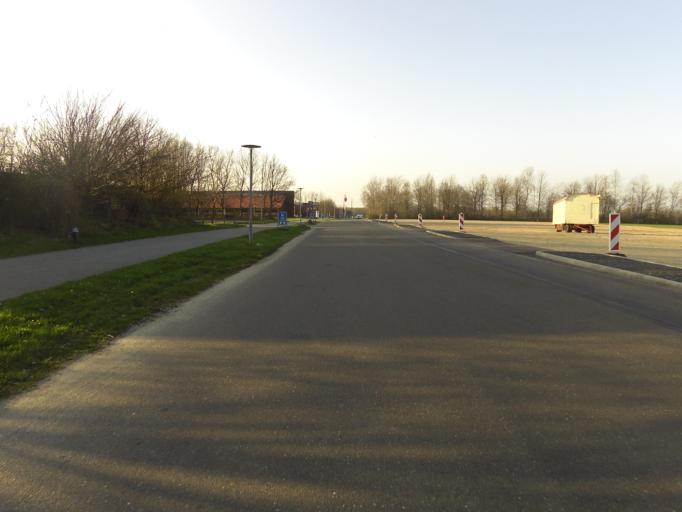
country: DK
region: South Denmark
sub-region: Vejen Kommune
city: Vejen
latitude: 55.4720
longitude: 9.1211
